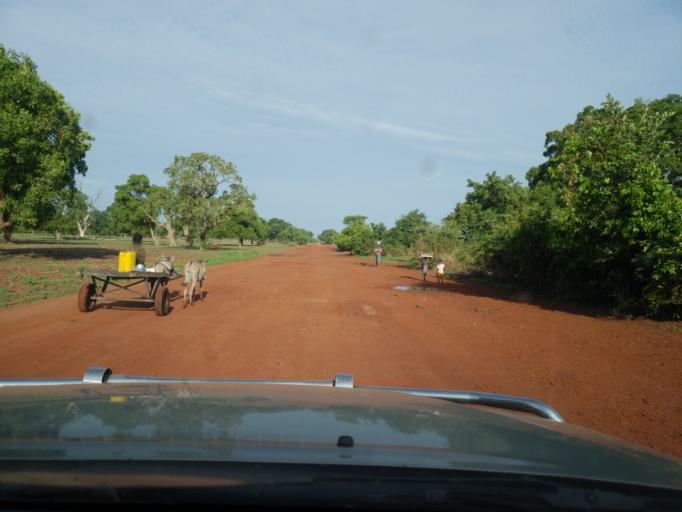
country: ML
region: Sikasso
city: Koutiala
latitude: 12.4197
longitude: -5.6992
